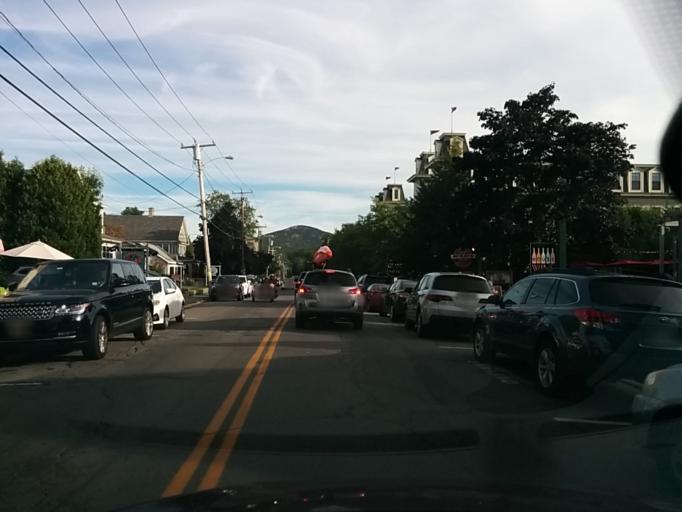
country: US
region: Maine
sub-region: Hancock County
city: Bar Harbor
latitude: 44.3864
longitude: -68.2040
